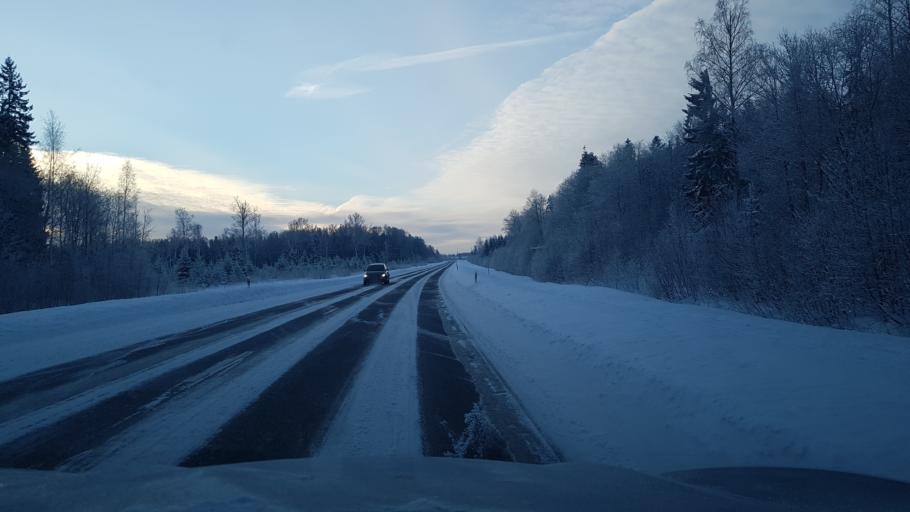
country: EE
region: Ida-Virumaa
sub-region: Johvi vald
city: Johvi
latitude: 59.3520
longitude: 27.4674
